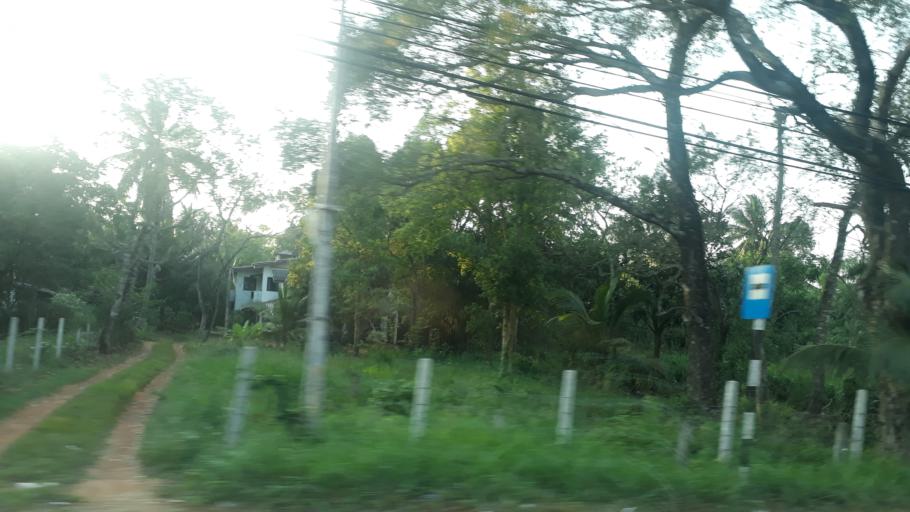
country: LK
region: North Central
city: Anuradhapura
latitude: 8.3008
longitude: 80.3767
